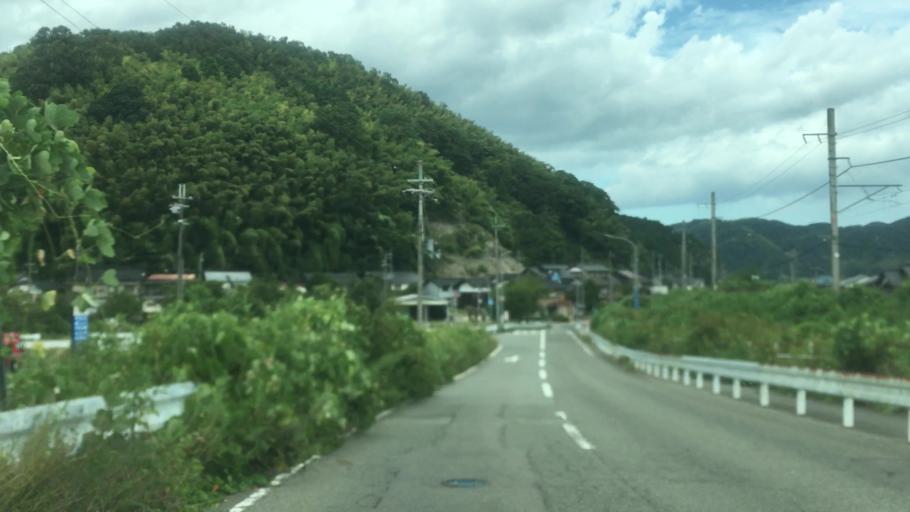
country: JP
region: Hyogo
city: Toyooka
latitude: 35.5649
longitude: 134.8034
